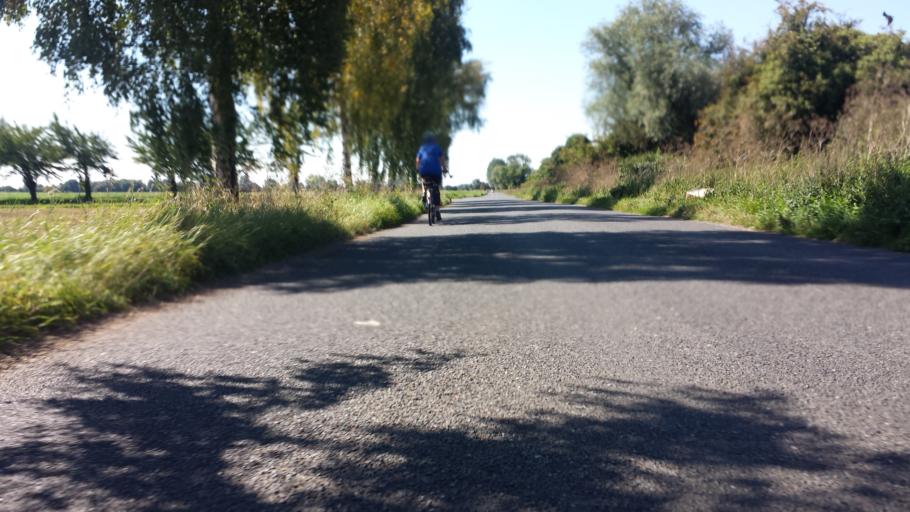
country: GB
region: England
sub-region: Cambridgeshire
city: Isleham
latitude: 52.3482
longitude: 0.3937
